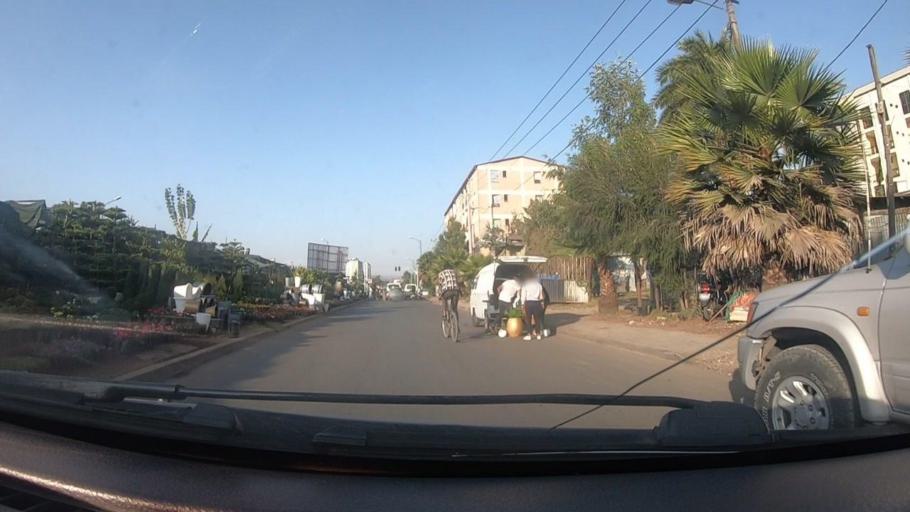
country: ET
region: Adis Abeba
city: Addis Ababa
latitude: 8.9950
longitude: 38.7537
